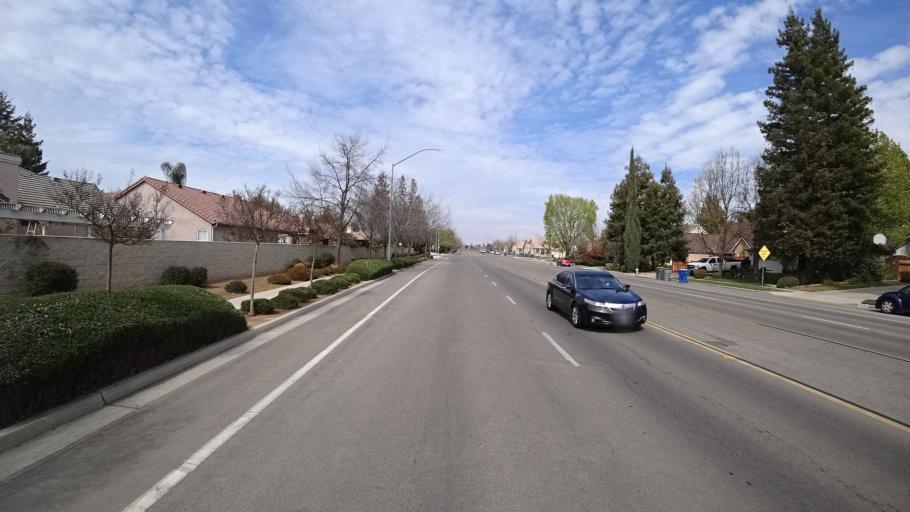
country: US
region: California
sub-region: Fresno County
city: West Park
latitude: 36.8252
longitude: -119.8747
